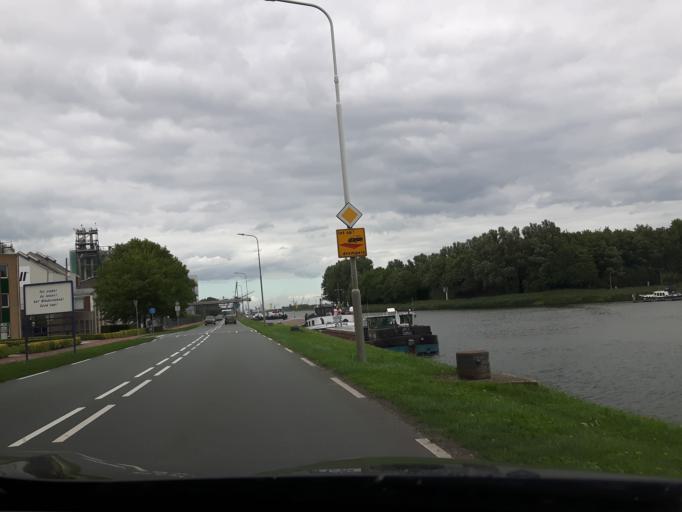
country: NL
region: Zeeland
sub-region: Gemeente Terneuzen
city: Sas van Gent
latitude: 51.2319
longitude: 3.8021
